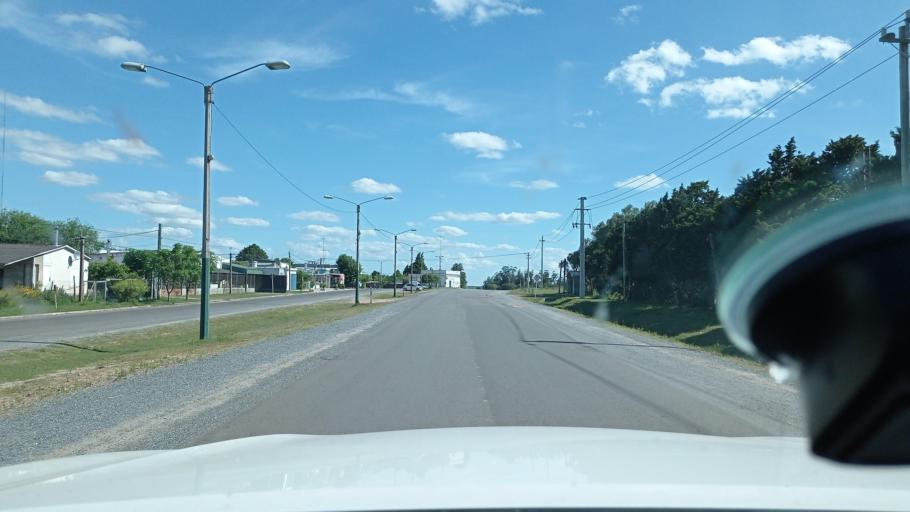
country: UY
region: Florida
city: Florida
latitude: -34.0896
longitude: -56.2384
